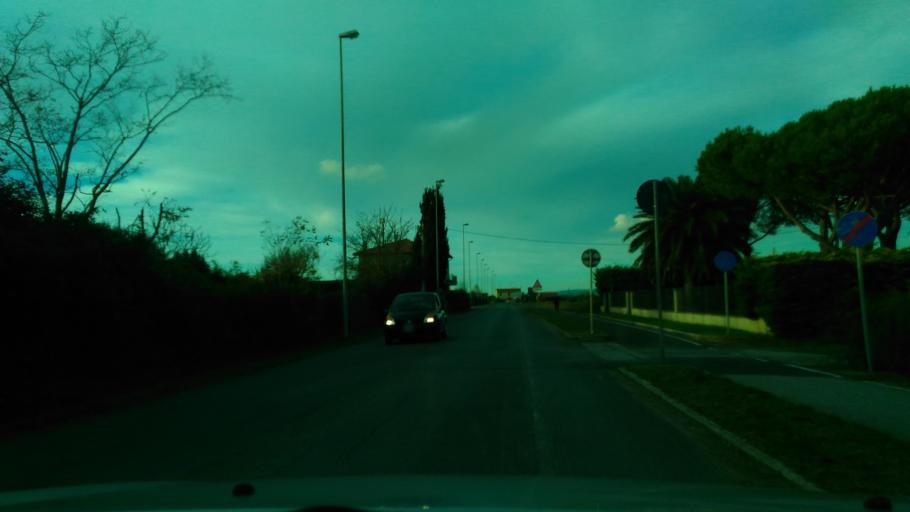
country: IT
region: Tuscany
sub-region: Provincia di Livorno
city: S.P. in Palazzi
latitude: 43.3083
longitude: 10.4894
